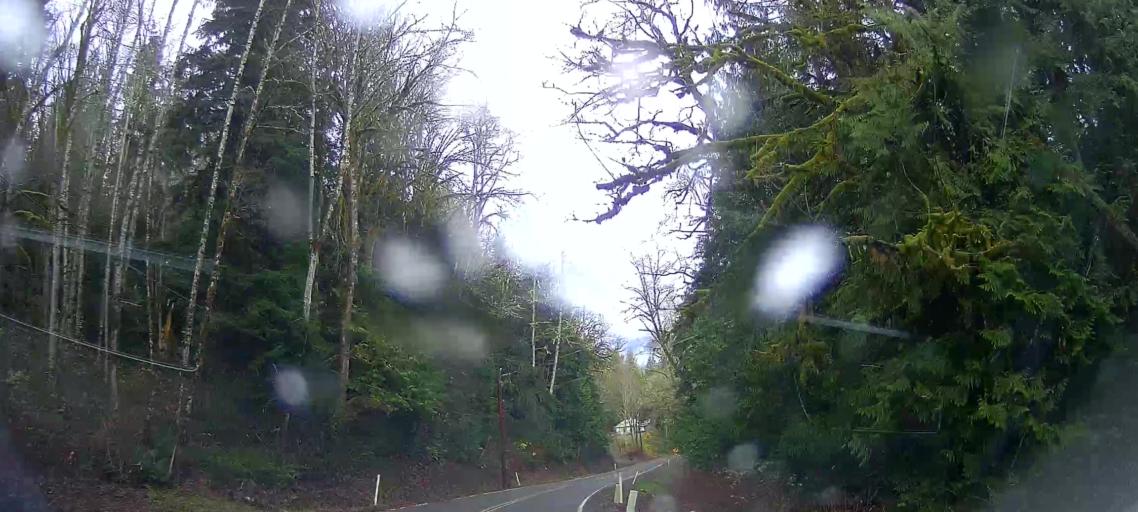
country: US
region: Washington
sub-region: Skagit County
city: Clear Lake
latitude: 48.4811
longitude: -122.1377
